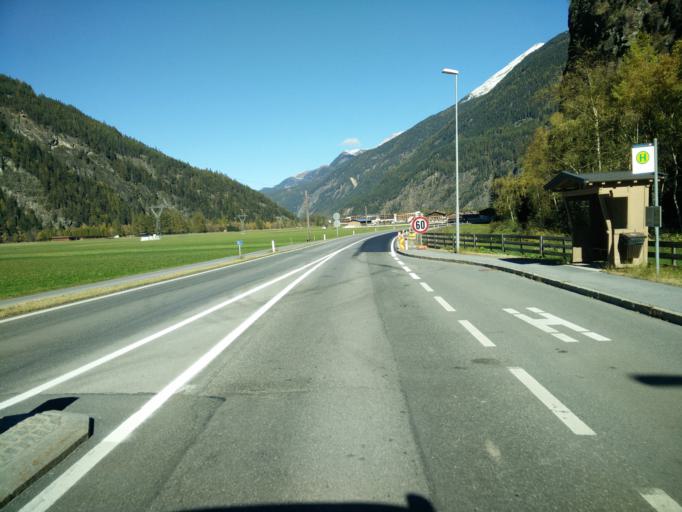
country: AT
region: Tyrol
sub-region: Politischer Bezirk Imst
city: Umhausen
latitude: 47.0584
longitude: 10.9651
